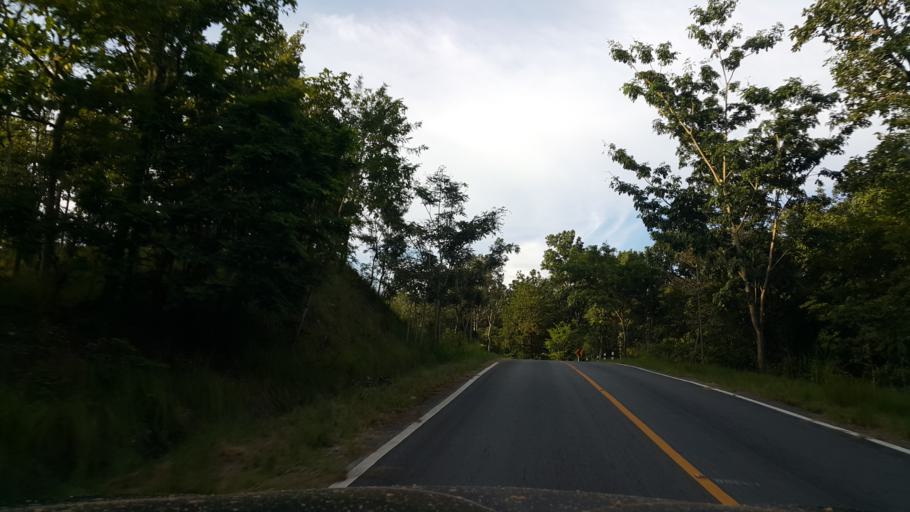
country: TH
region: Mae Hong Son
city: Mae Hi
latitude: 19.1831
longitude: 98.4114
